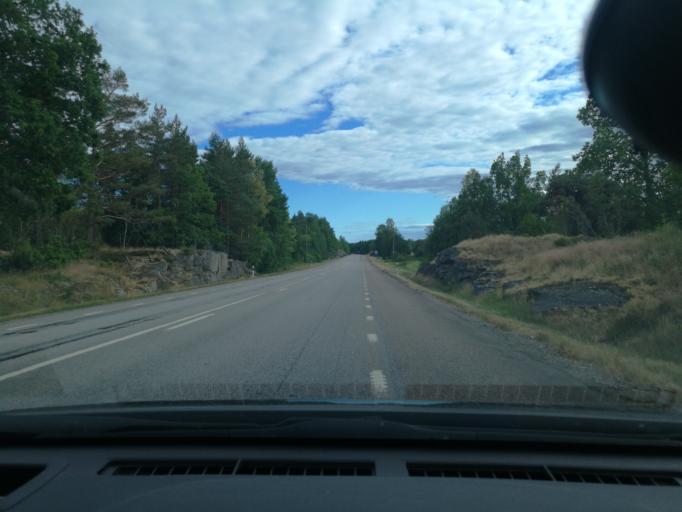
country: SE
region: Kalmar
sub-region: Vasterviks Kommun
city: Ankarsrum
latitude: 57.5827
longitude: 16.4853
